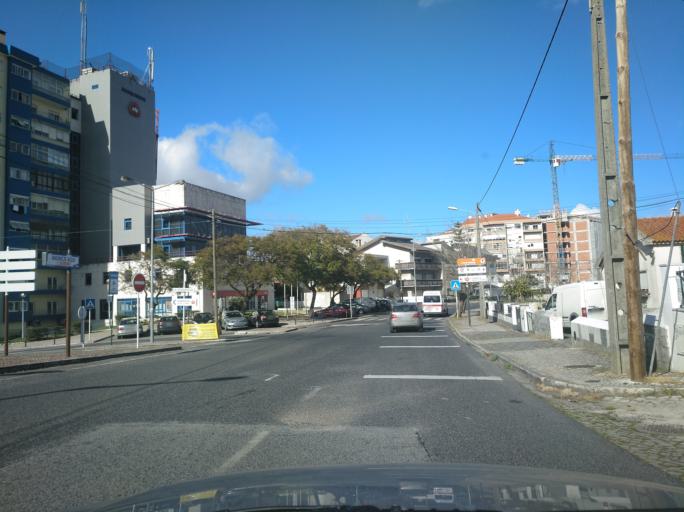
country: PT
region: Lisbon
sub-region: Loures
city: Loures
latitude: 38.8259
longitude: -9.1706
